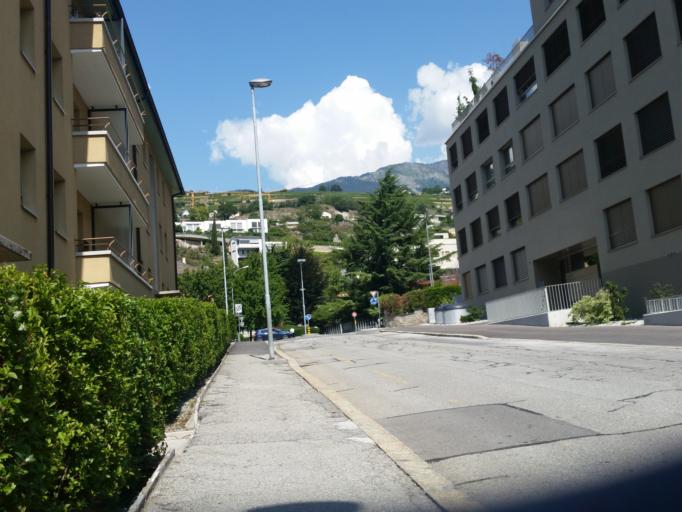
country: CH
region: Valais
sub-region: Sion District
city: Sitten
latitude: 46.2295
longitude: 7.3491
